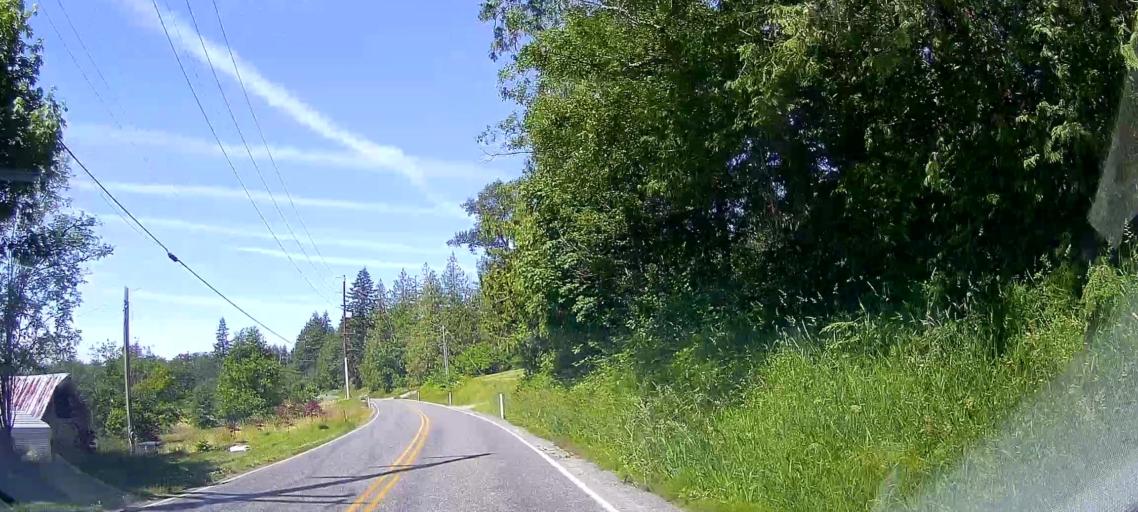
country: US
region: Washington
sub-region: Skagit County
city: Burlington
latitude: 48.5349
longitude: -122.2966
